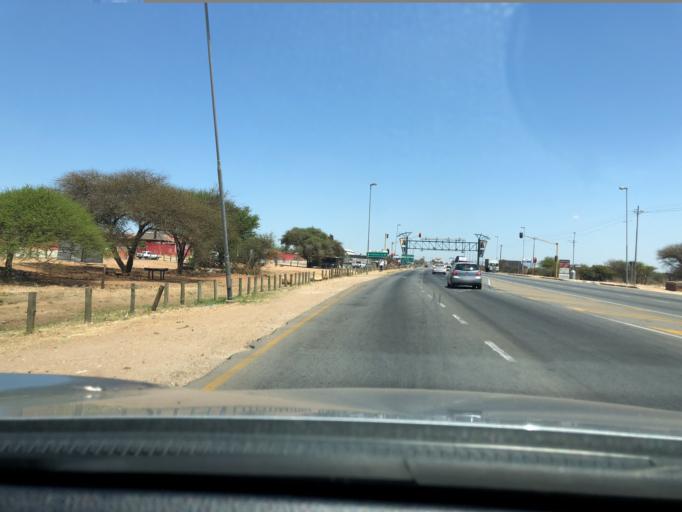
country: ZA
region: Limpopo
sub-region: Capricorn District Municipality
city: Polokwane
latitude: -23.8698
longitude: 29.4659
